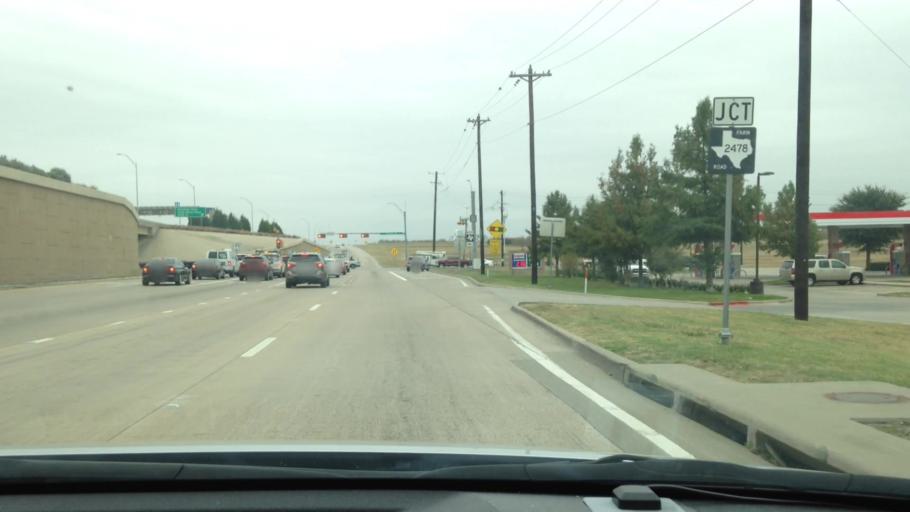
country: US
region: Texas
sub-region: Collin County
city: Allen
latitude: 33.1242
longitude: -96.7339
